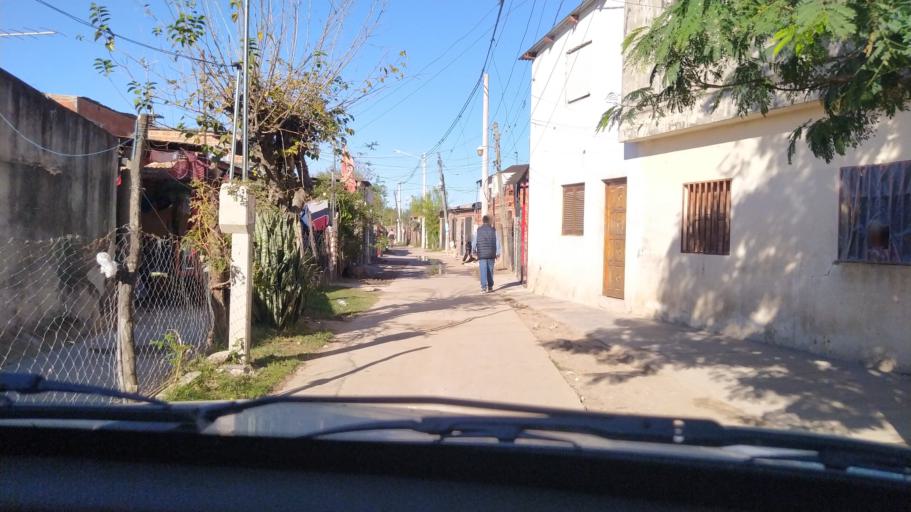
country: AR
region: Corrientes
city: Corrientes
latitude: -27.4938
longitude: -58.8080
